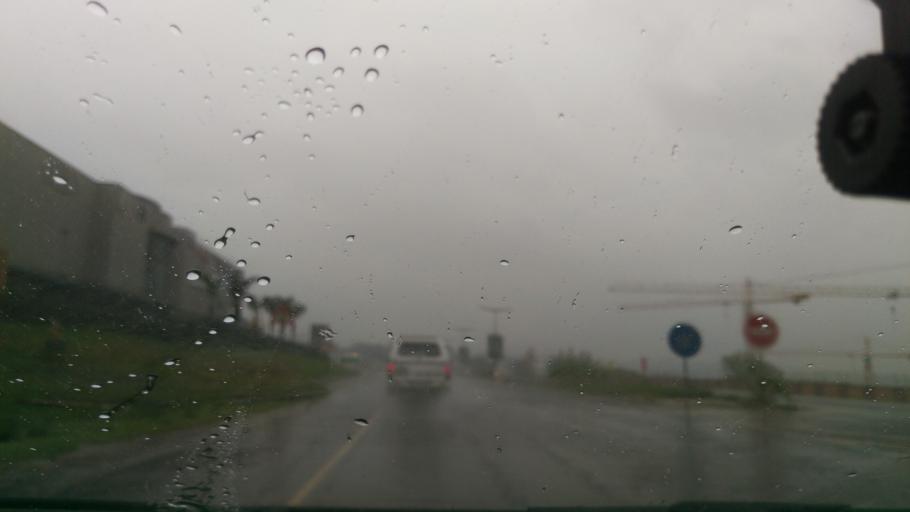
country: ZA
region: Gauteng
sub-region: West Rand District Municipality
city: Muldersdriseloop
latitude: -26.0565
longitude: 27.9457
